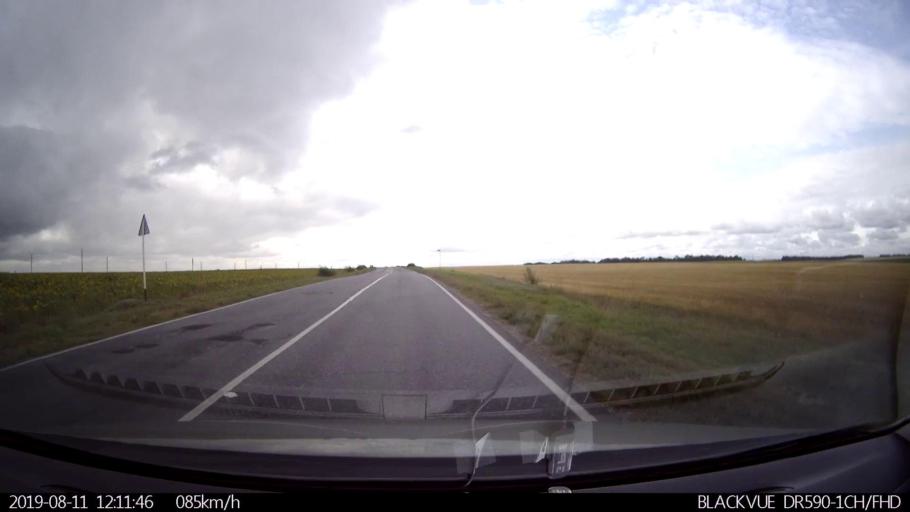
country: RU
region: Ulyanovsk
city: Silikatnyy
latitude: 53.9815
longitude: 48.0007
